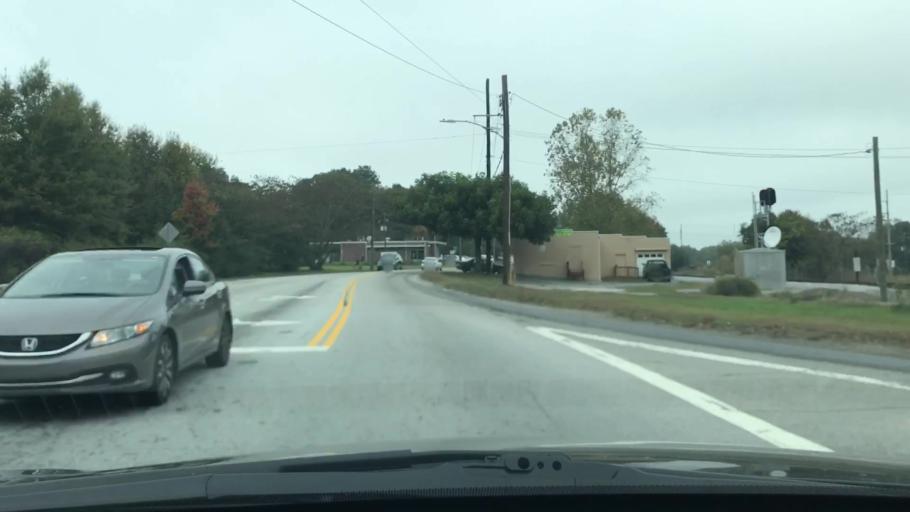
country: US
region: Georgia
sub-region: DeKalb County
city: Scottdale
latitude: 33.7901
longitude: -84.2647
